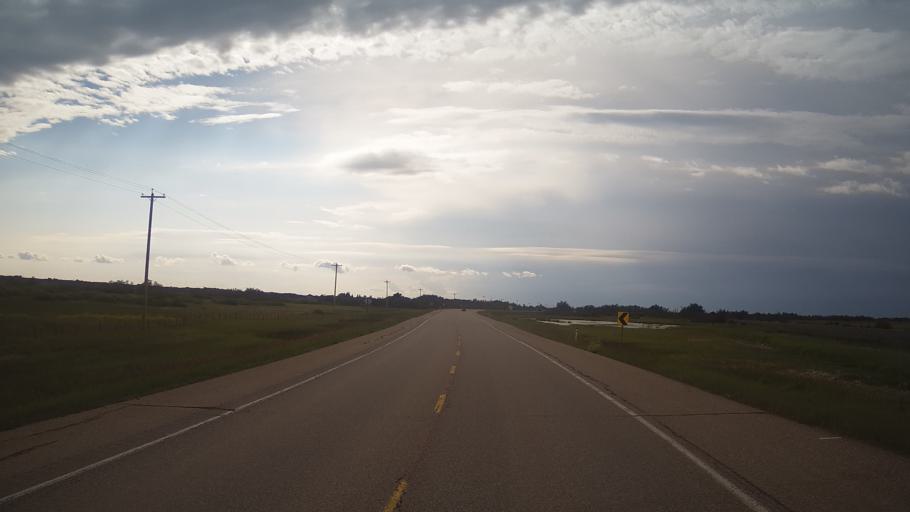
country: CA
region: Alberta
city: Viking
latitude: 53.1311
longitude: -111.9067
